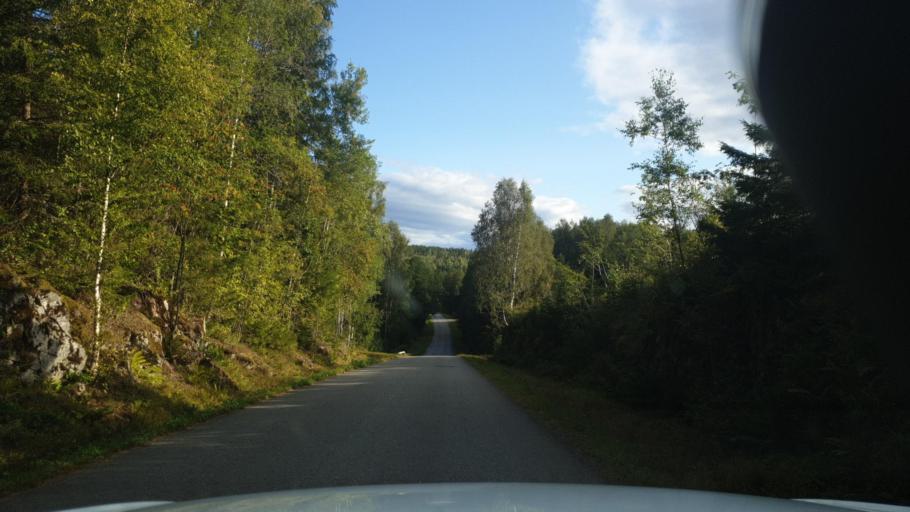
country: SE
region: Vaermland
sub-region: Eda Kommun
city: Amotfors
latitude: 59.8176
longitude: 12.3626
